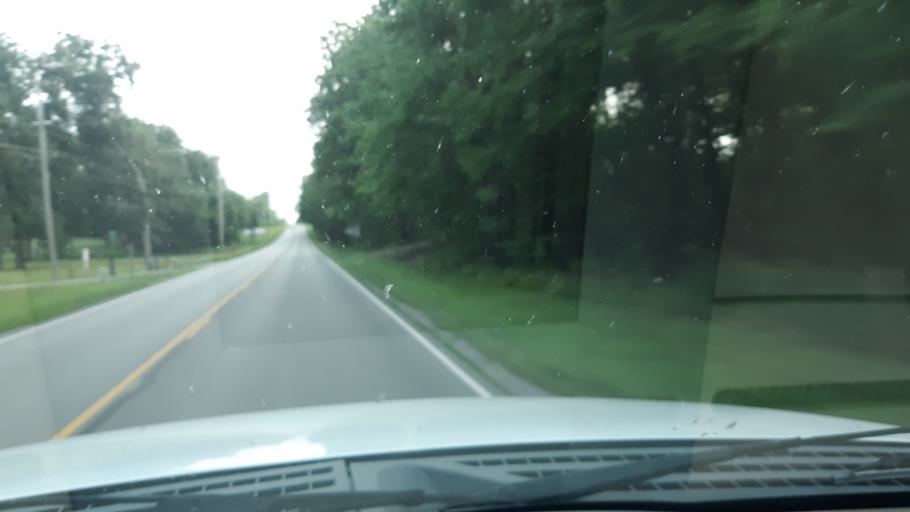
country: US
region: Illinois
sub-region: White County
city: Norris City
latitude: 37.9595
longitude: -88.3351
